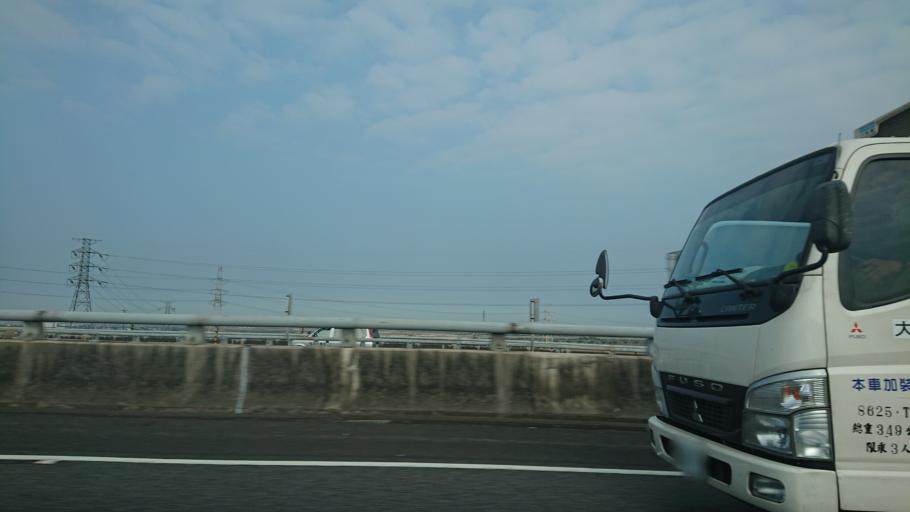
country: TW
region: Taiwan
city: Fengyuan
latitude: 24.3071
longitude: 120.6131
